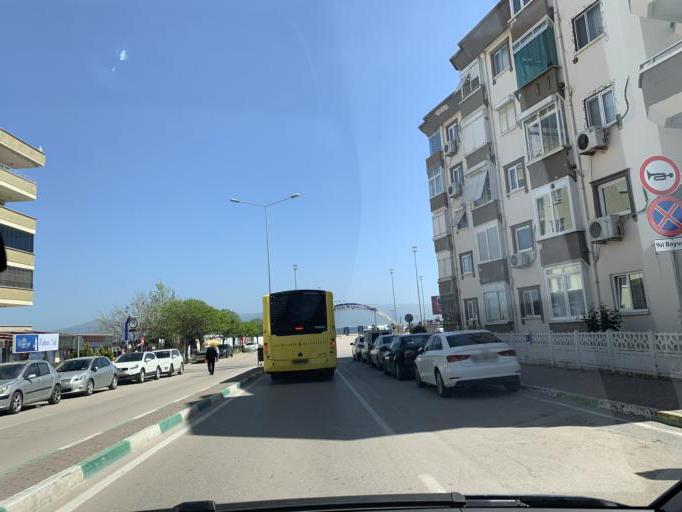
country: TR
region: Bursa
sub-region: Mudanya
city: Mudanya
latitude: 40.3551
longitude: 28.9262
